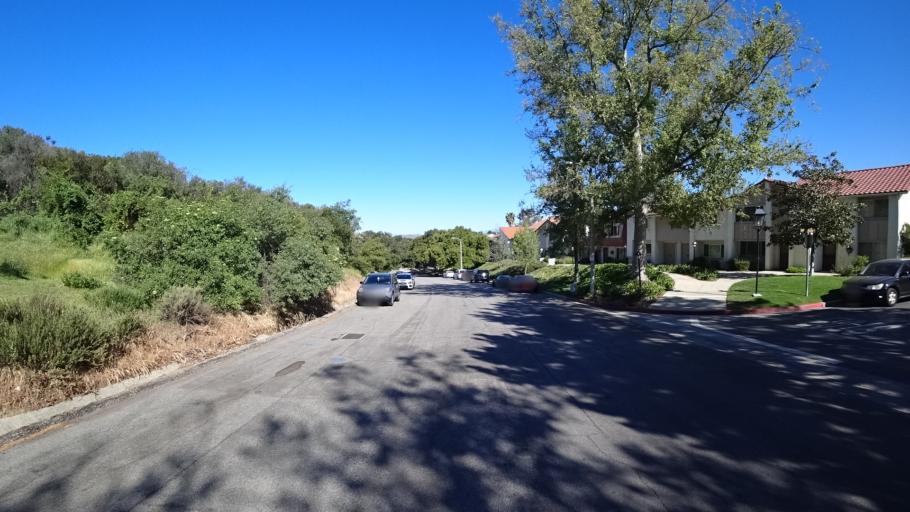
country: US
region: California
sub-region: Ventura County
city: Thousand Oaks
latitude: 34.1746
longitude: -118.8823
